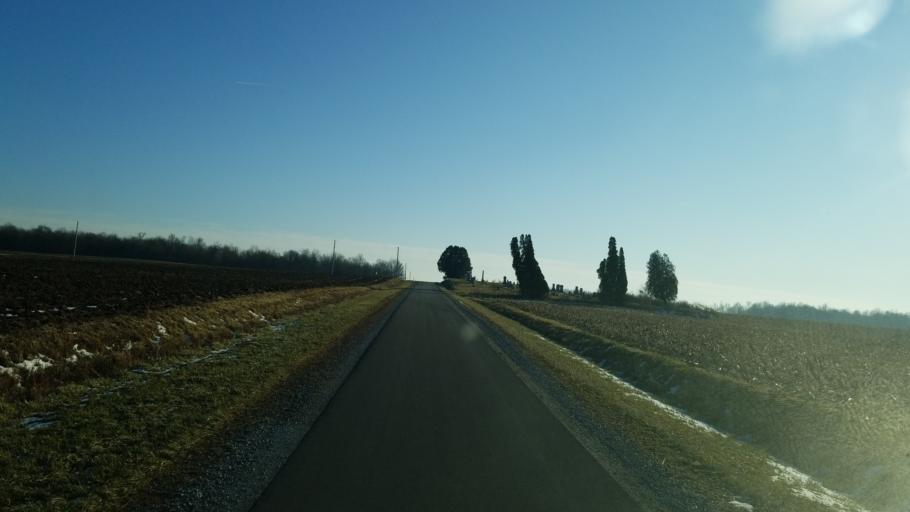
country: US
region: Ohio
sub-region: Crawford County
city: Bucyrus
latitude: 40.9891
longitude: -82.9587
